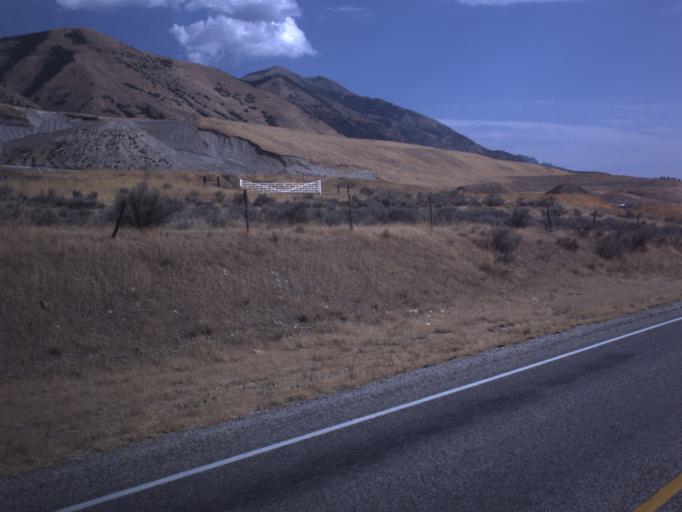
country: US
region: Utah
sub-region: Box Elder County
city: Garland
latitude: 41.7487
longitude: -112.0992
